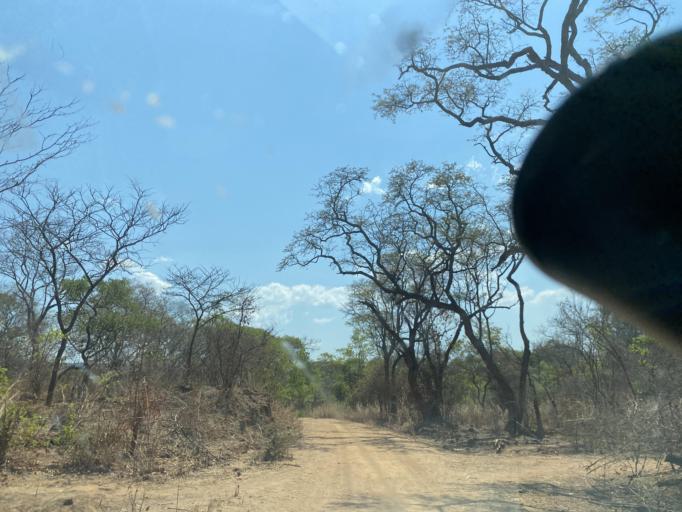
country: ZM
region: Lusaka
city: Chongwe
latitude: -15.0877
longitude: 29.4948
